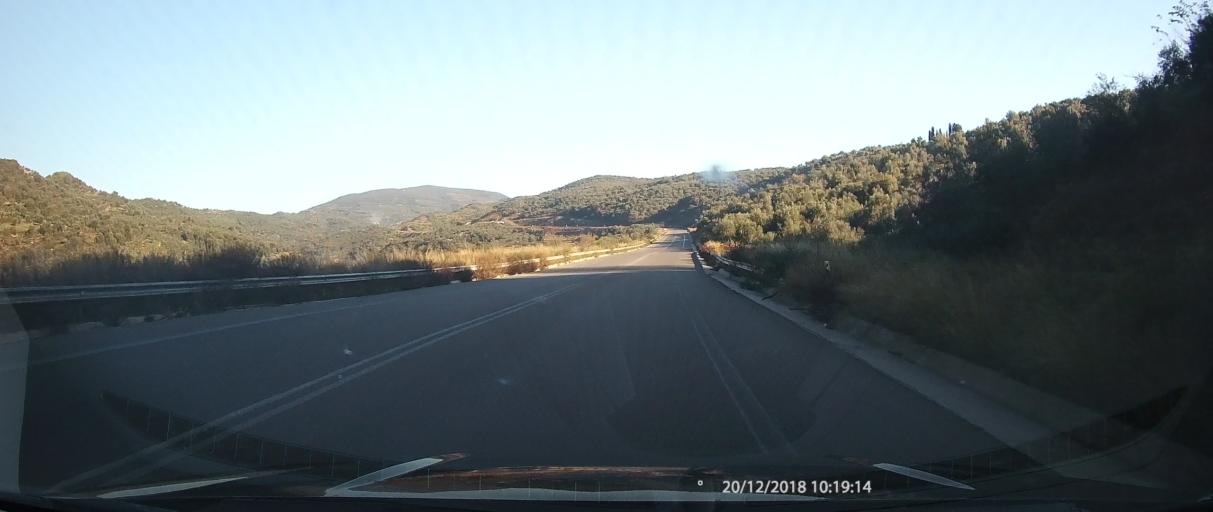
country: GR
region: Peloponnese
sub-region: Nomos Lakonias
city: Magoula
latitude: 37.1312
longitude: 22.4201
